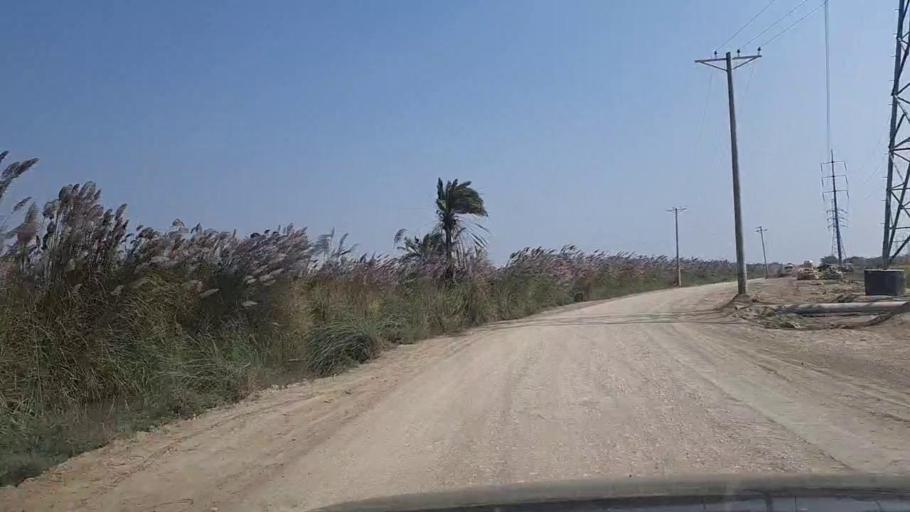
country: PK
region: Sindh
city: Gharo
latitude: 24.7219
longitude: 67.5531
